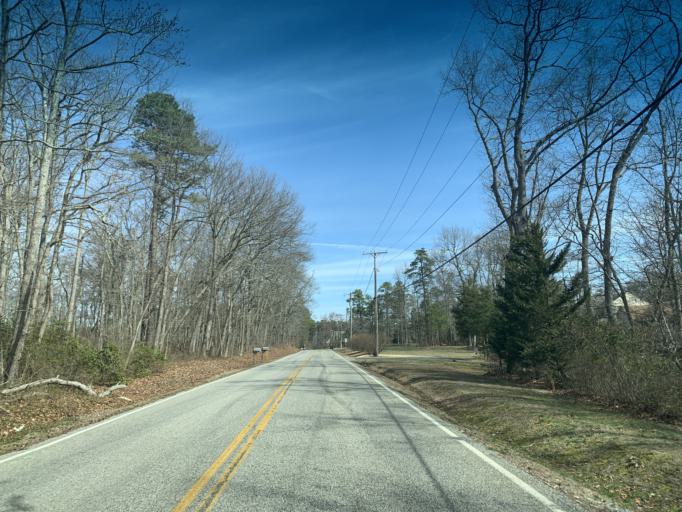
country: US
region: Maryland
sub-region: Cecil County
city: Charlestown
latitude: 39.5733
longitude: -75.9874
